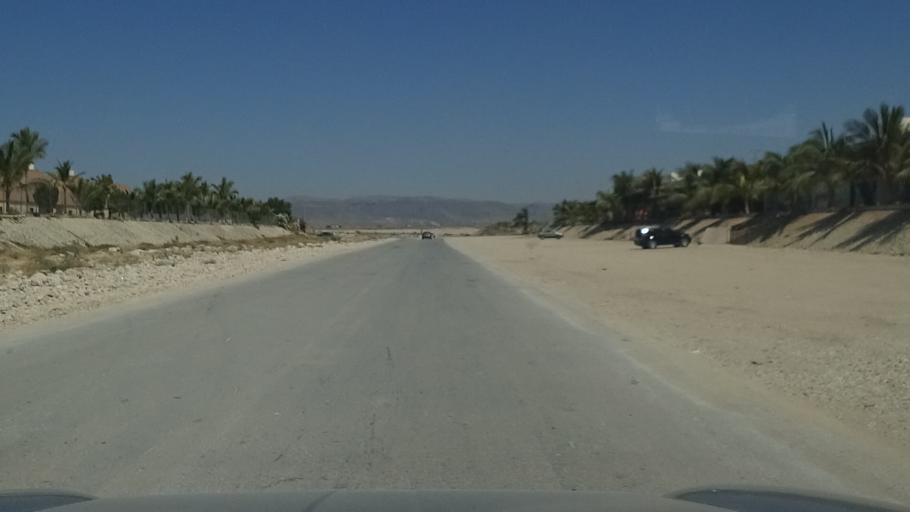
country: OM
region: Zufar
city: Salalah
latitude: 17.0214
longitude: 54.0632
